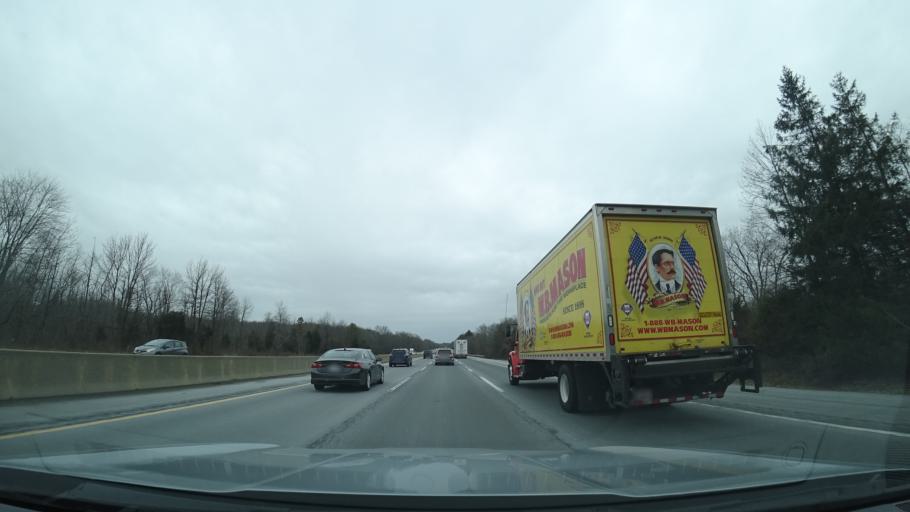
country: US
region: New Jersey
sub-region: Burlington County
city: Roebling
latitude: 40.0687
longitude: -74.7636
